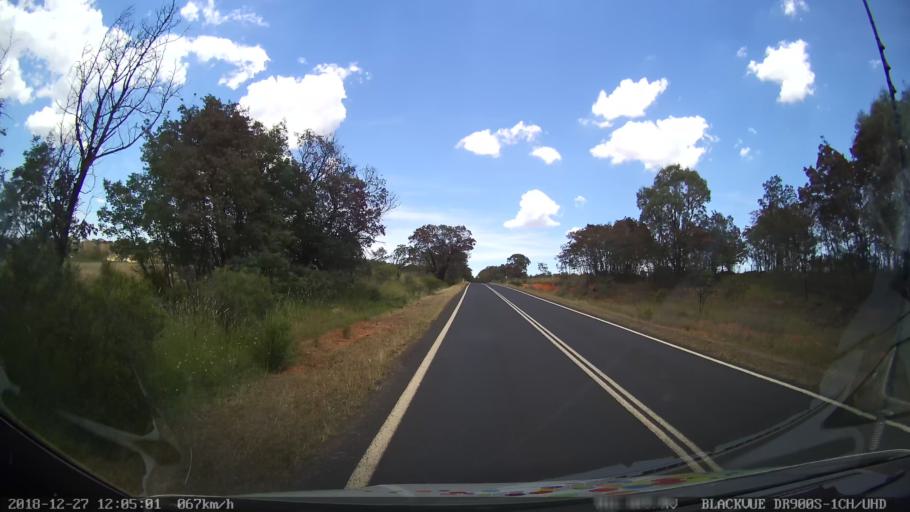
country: AU
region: New South Wales
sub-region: Blayney
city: Blayney
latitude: -33.7999
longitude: 149.3432
